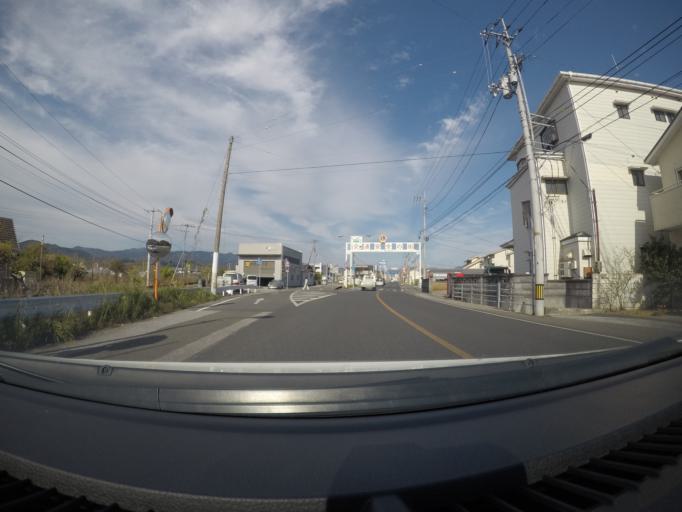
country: JP
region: Kochi
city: Kochi-shi
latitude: 33.6014
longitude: 133.6736
